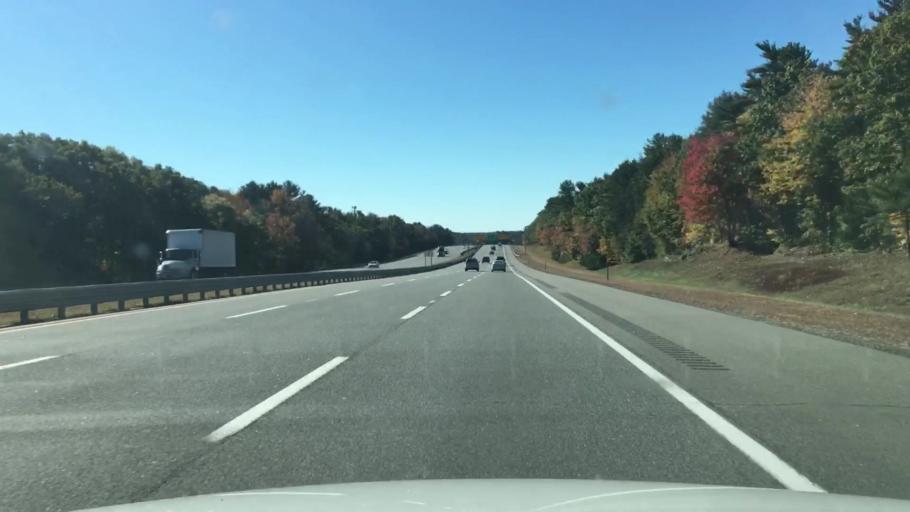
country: US
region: Maine
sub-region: York County
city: Cape Neddick
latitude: 43.1738
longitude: -70.6511
